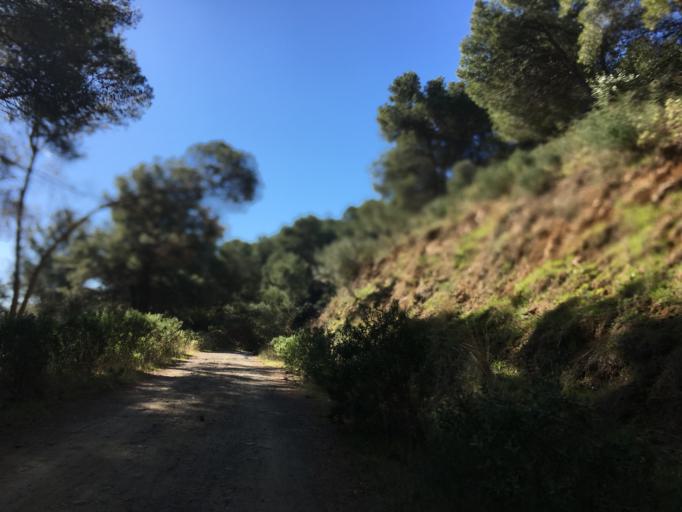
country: ES
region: Andalusia
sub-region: Provincia de Malaga
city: Malaga
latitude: 36.8056
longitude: -4.4041
